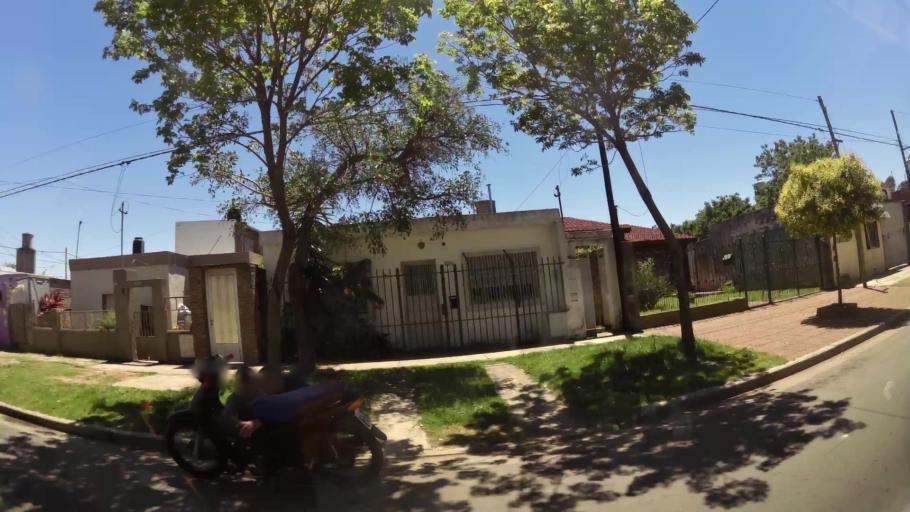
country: AR
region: Santa Fe
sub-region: Departamento de Rosario
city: Rosario
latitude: -32.9544
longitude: -60.7081
